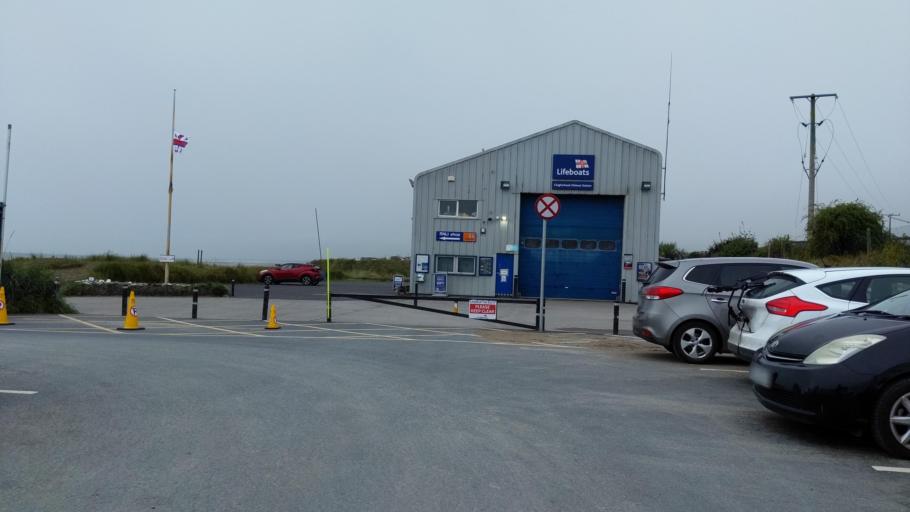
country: IE
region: Leinster
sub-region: Lu
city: Clogherhead
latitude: 53.7886
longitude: -6.2349
